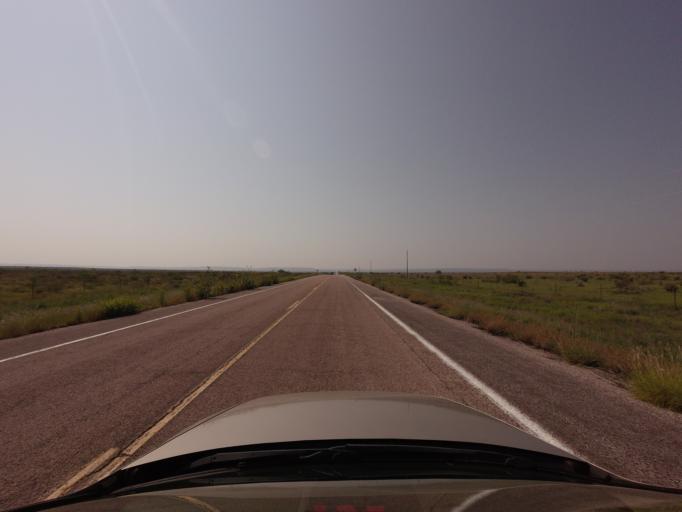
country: US
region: New Mexico
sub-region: Quay County
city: Tucumcari
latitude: 34.9463
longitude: -103.7602
